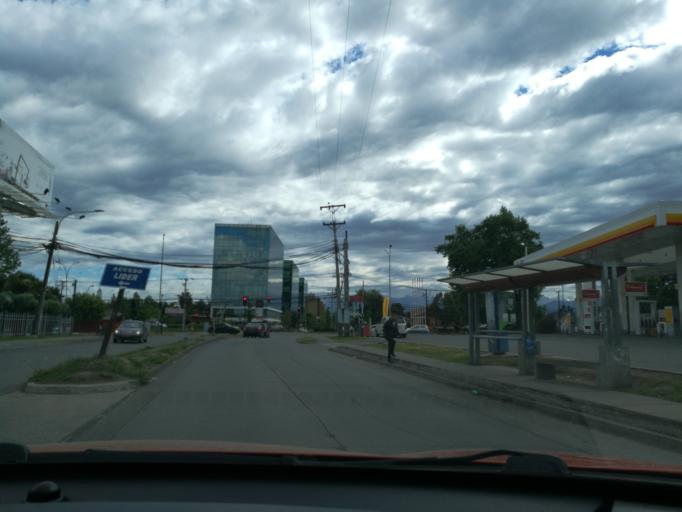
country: CL
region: O'Higgins
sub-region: Provincia de Cachapoal
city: Rancagua
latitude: -34.1822
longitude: -70.7301
